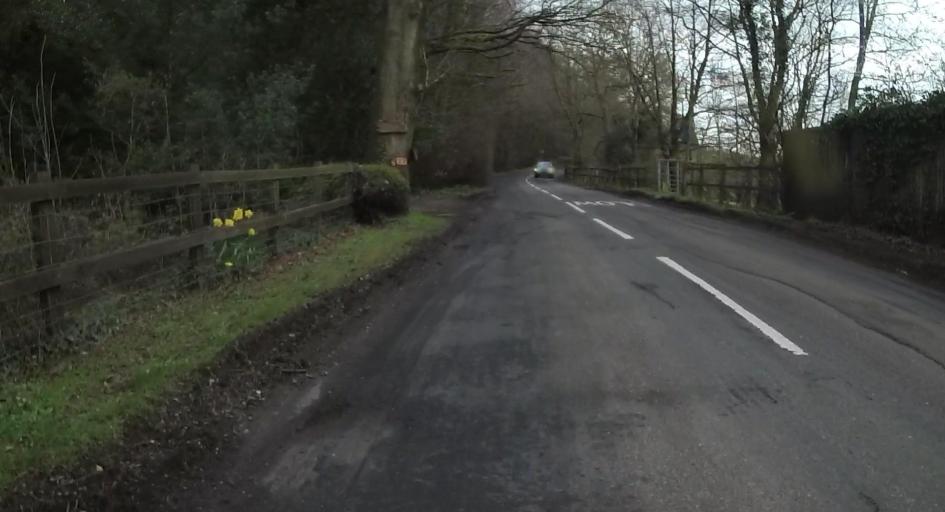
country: GB
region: England
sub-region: Hampshire
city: Alton
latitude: 51.1831
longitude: -0.9866
